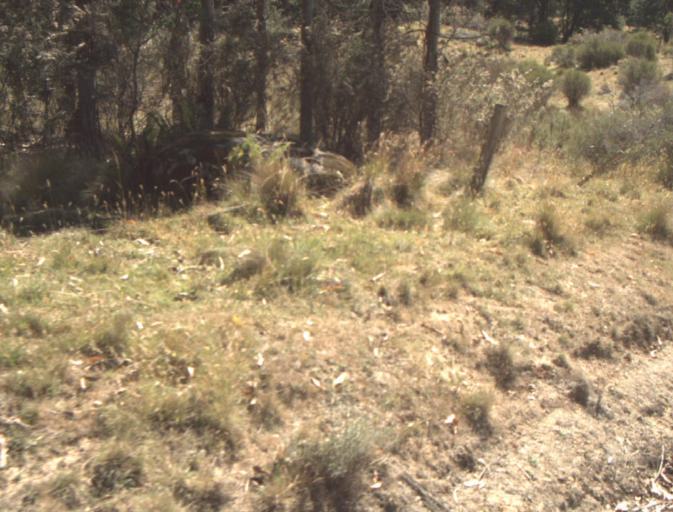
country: AU
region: Tasmania
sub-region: Dorset
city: Scottsdale
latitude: -41.3616
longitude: 147.4619
